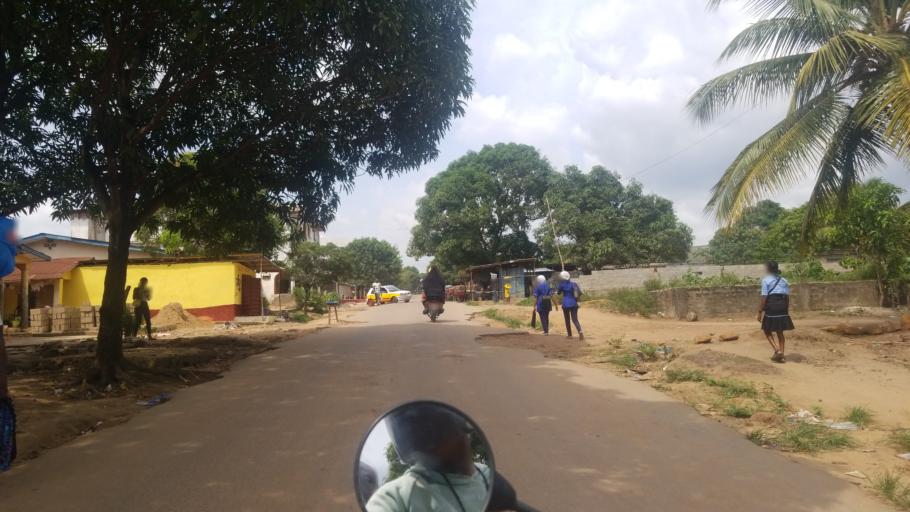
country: SL
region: Western Area
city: Waterloo
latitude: 8.3307
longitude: -13.0465
